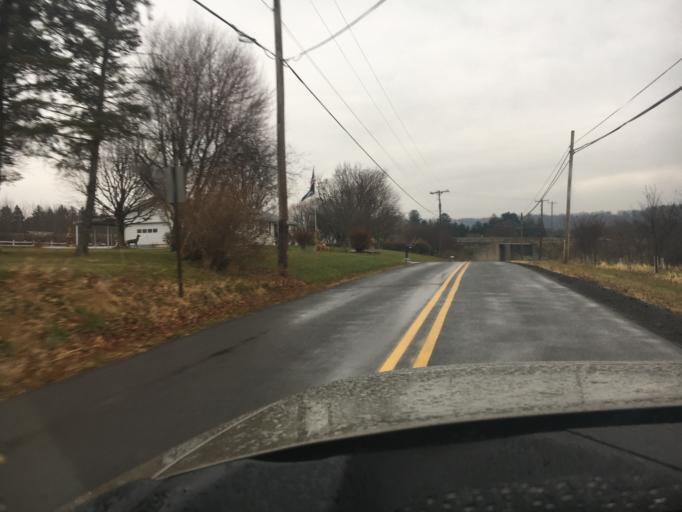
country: US
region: Pennsylvania
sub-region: Luzerne County
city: Conyngham
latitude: 41.0277
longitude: -76.0128
